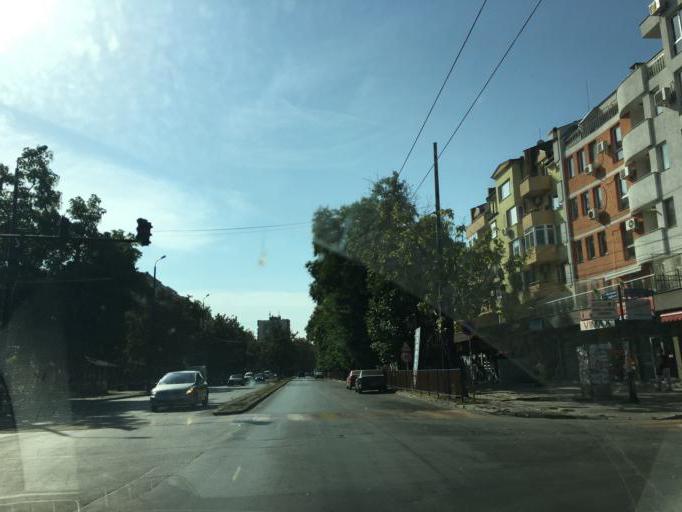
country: BG
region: Pazardzhik
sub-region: Obshtina Pazardzhik
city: Pazardzhik
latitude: 42.2031
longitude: 24.3310
